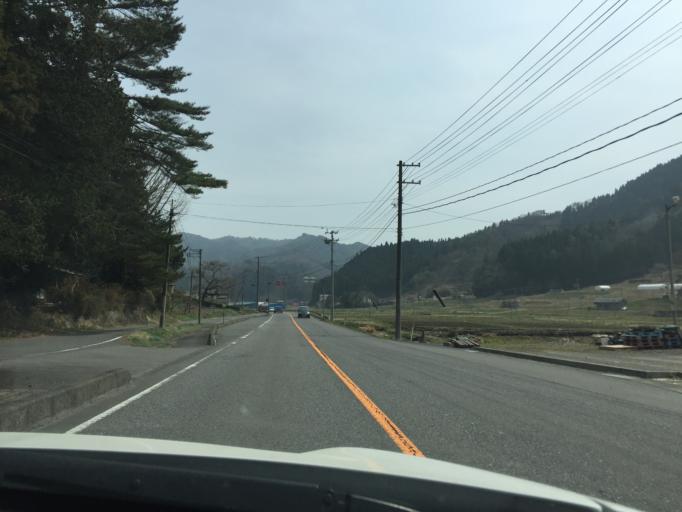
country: JP
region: Fukushima
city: Ishikawa
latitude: 37.0877
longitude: 140.5163
